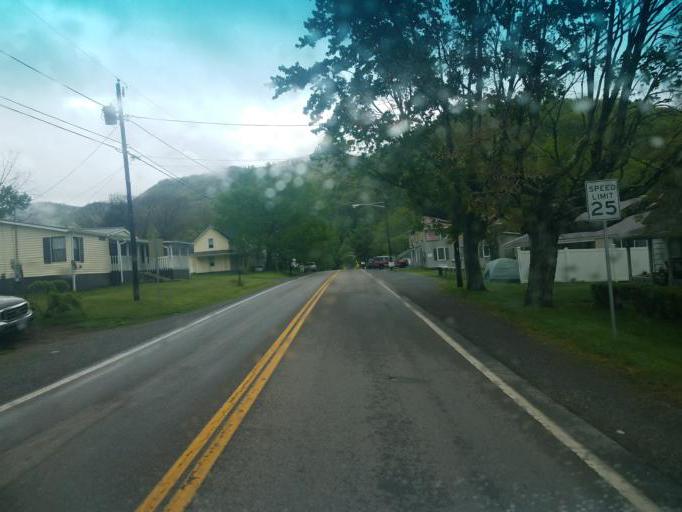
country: US
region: Virginia
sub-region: Washington County
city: Emory
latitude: 36.6330
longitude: -81.7835
